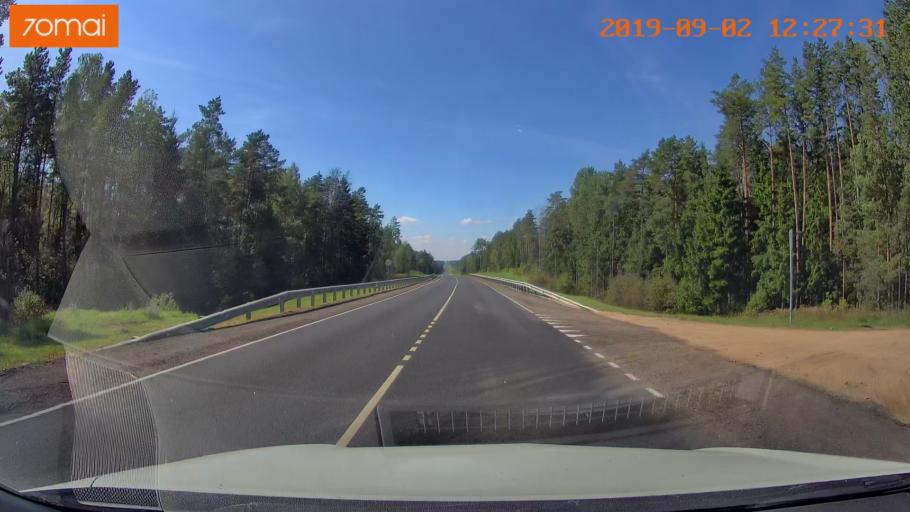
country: RU
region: Smolensk
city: Shumyachi
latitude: 53.8529
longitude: 32.5418
